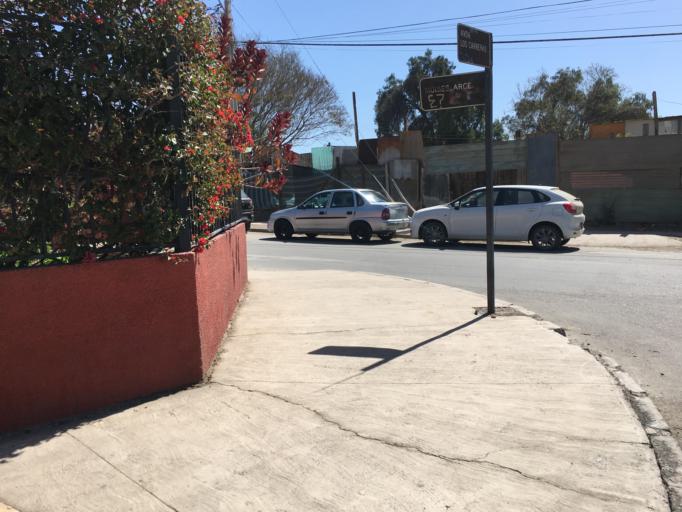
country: CL
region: Atacama
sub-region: Provincia de Copiapo
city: Copiapo
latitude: -27.4104
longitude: -70.2854
